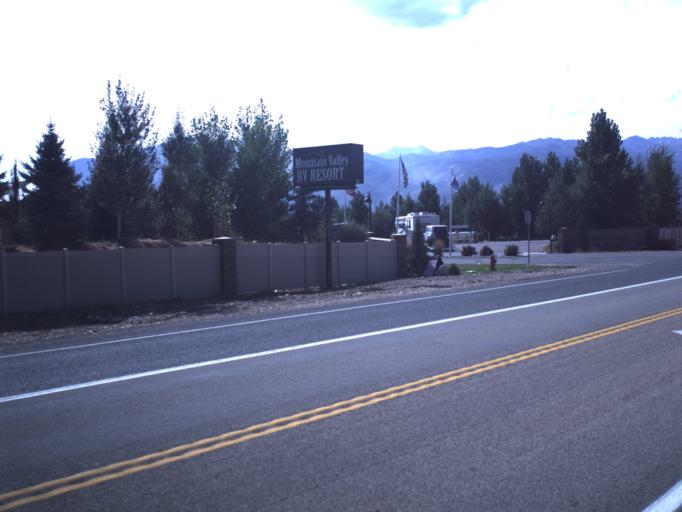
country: US
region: Utah
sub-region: Wasatch County
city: Heber
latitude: 40.4812
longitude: -111.4012
